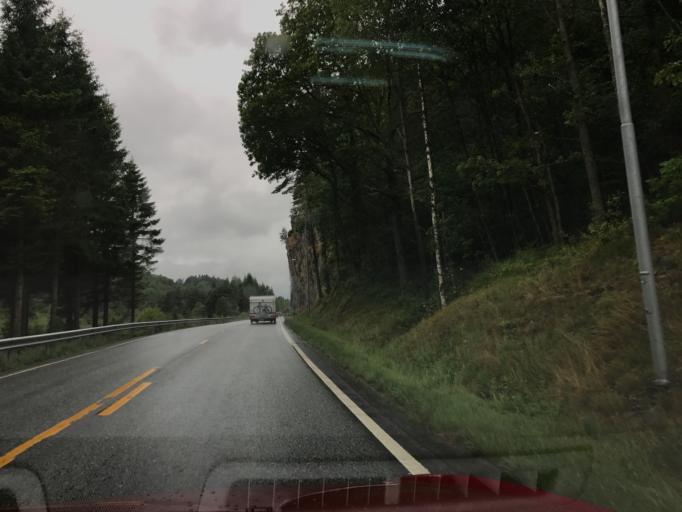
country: NO
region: Vest-Agder
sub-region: Lyngdal
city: Lyngdal
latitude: 58.1505
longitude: 7.1501
